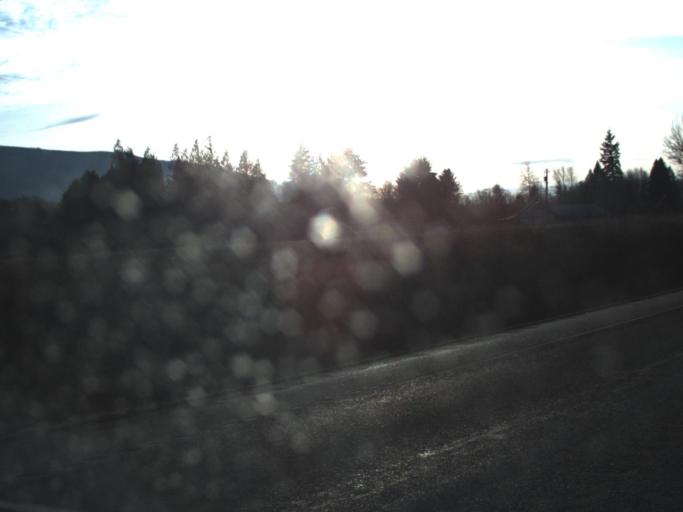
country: US
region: Washington
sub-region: Skagit County
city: Sedro-Woolley
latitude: 48.5281
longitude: -122.0989
